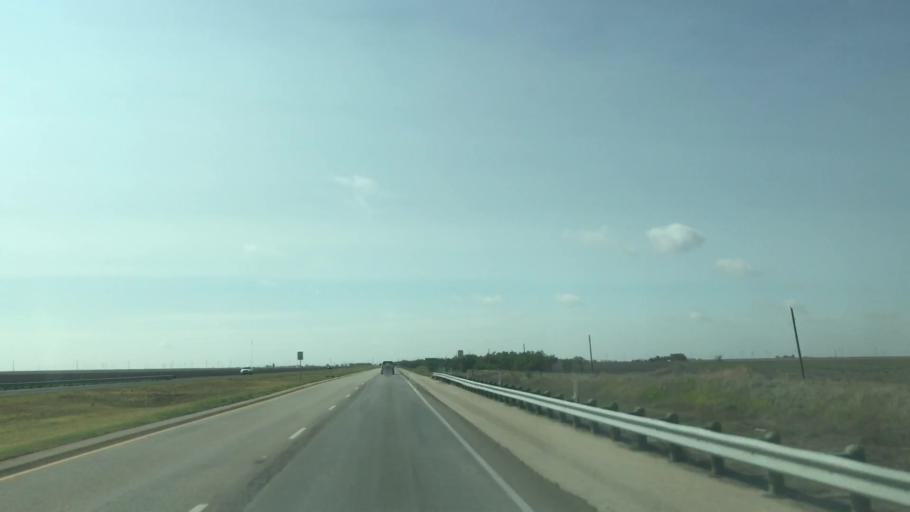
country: US
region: Texas
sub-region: Scurry County
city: Snyder
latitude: 32.5865
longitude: -100.7292
